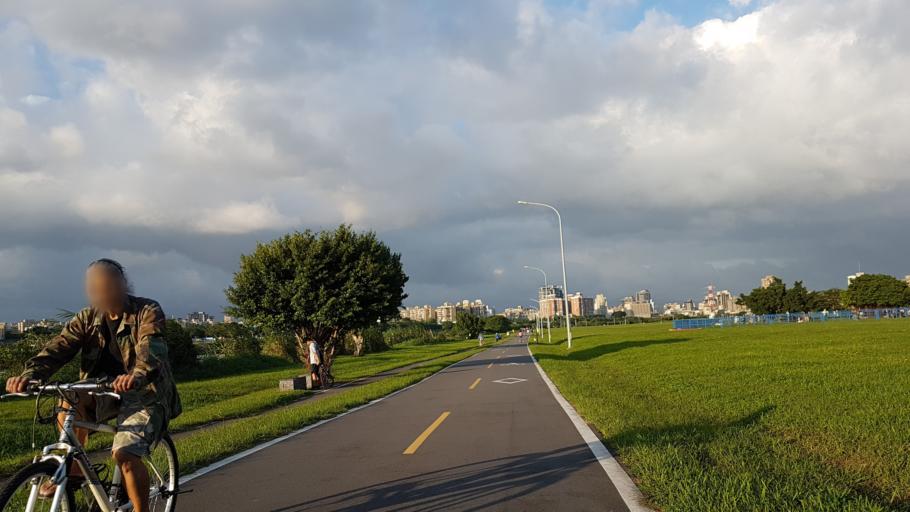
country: TW
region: Taipei
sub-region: Taipei
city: Banqiao
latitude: 25.0155
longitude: 121.5048
